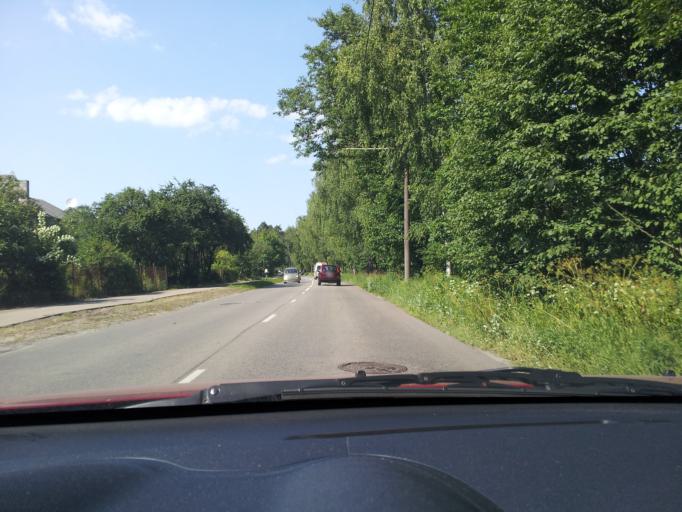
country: LV
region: Riga
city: Bolderaja
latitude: 57.0610
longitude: 24.1063
